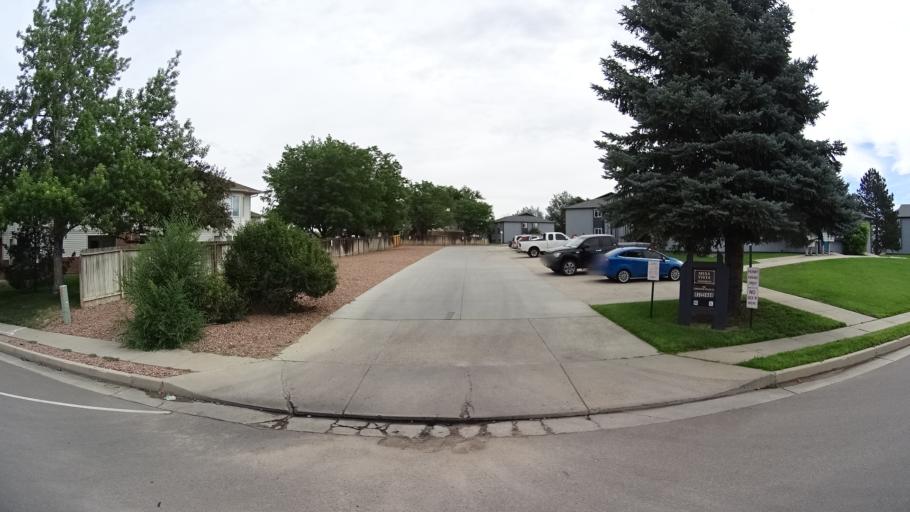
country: US
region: Colorado
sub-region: El Paso County
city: Fountain
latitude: 38.6967
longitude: -104.6994
